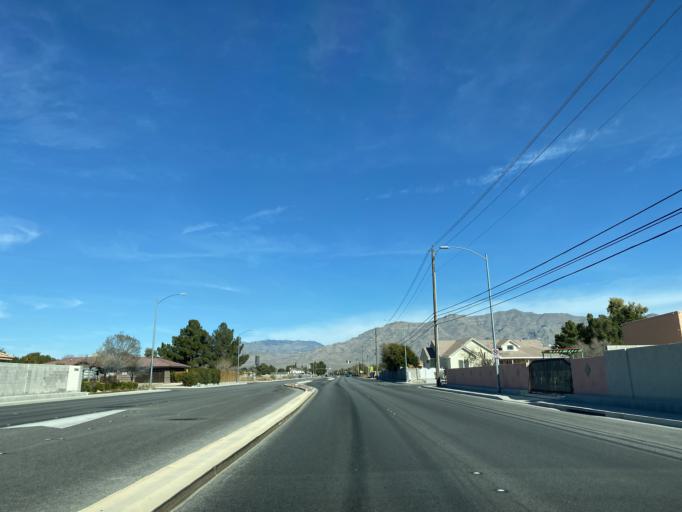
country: US
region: Nevada
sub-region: Clark County
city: North Las Vegas
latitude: 36.2984
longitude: -115.2240
